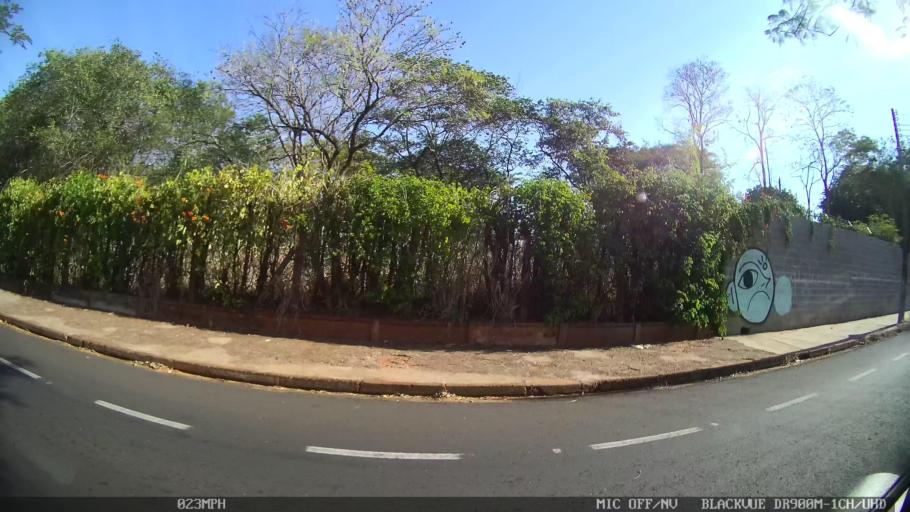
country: BR
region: Sao Paulo
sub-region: Sao Jose Do Rio Preto
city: Sao Jose do Rio Preto
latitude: -20.7841
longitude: -49.3579
